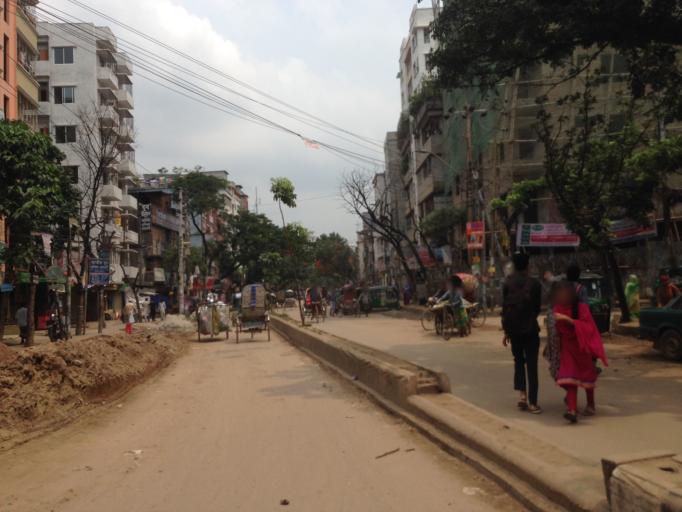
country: BD
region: Dhaka
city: Paltan
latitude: 23.7492
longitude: 90.4264
